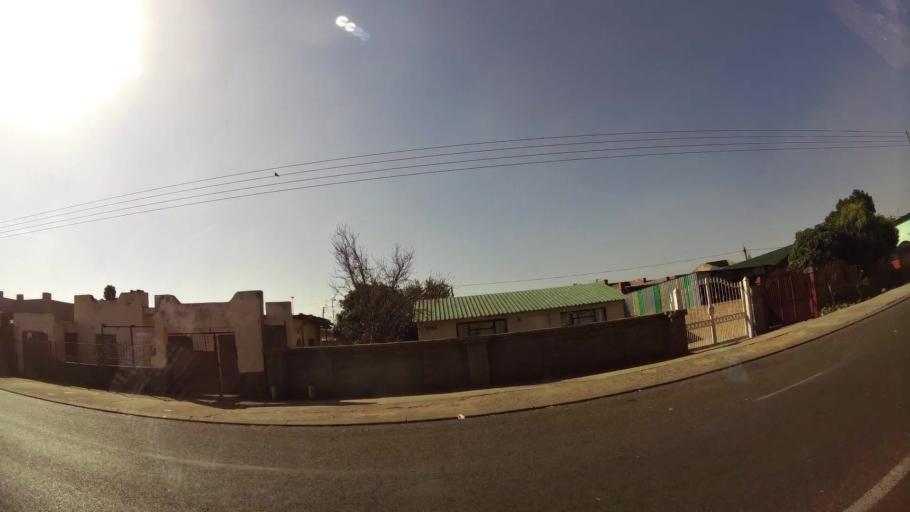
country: ZA
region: Gauteng
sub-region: City of Tshwane Metropolitan Municipality
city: Mabopane
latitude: -25.5351
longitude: 28.0975
